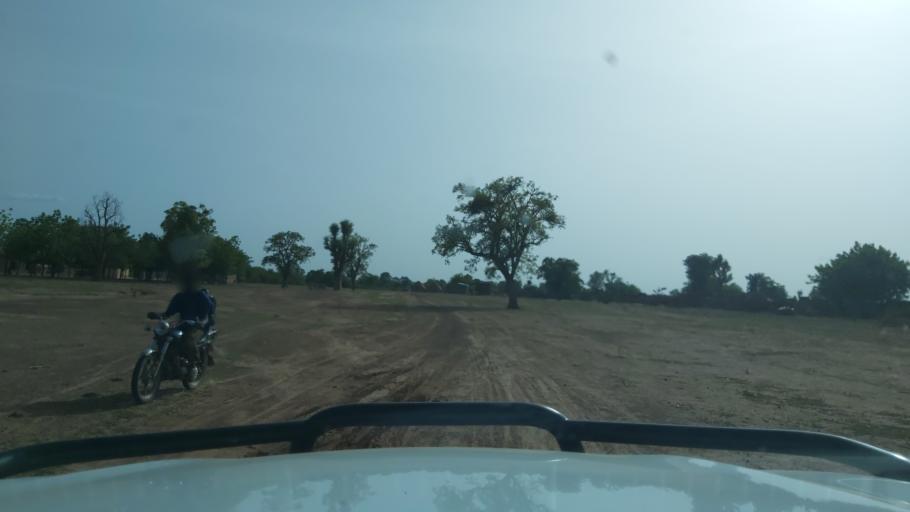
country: ML
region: Koulikoro
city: Koulikoro
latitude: 13.1653
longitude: -7.7927
